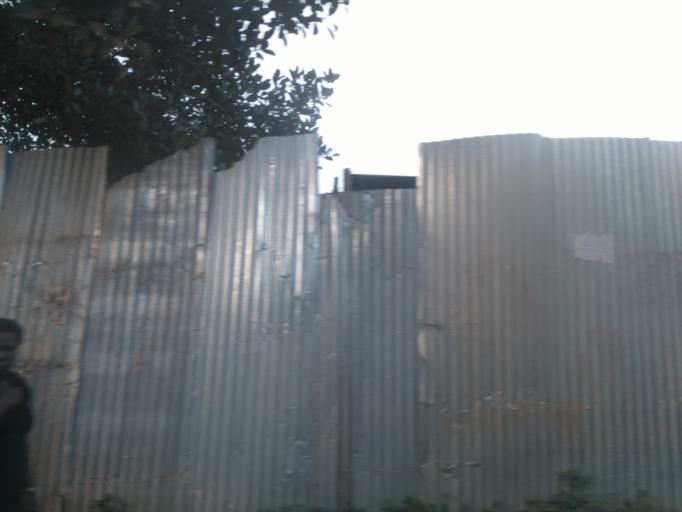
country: UG
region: Central Region
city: Kampala Central Division
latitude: 0.3439
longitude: 32.5791
